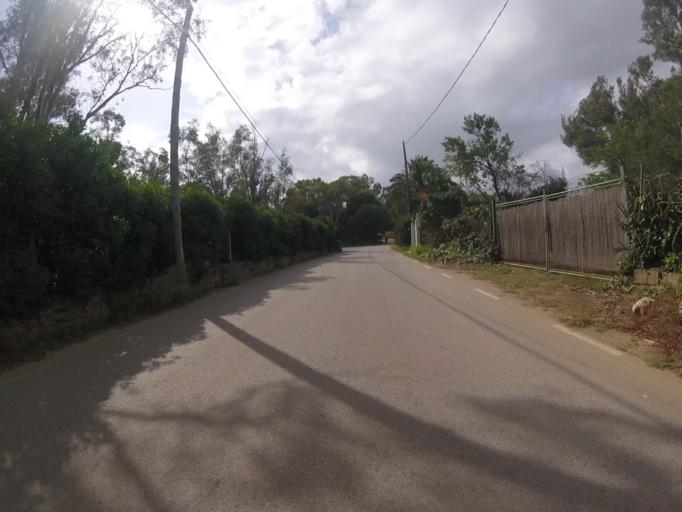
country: ES
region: Valencia
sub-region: Provincia de Castello
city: Orpesa/Oropesa del Mar
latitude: 40.1309
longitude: 0.1625
